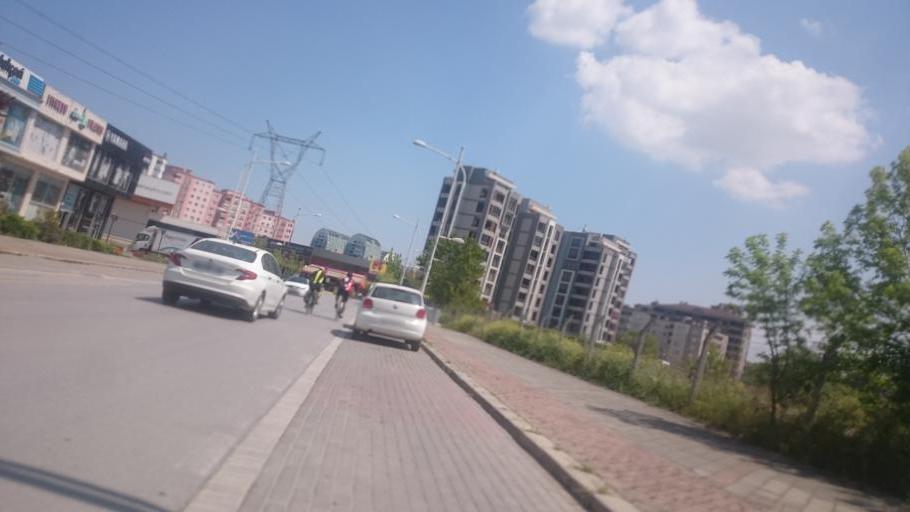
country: TR
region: Bursa
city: Cali
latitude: 40.2157
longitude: 28.8988
